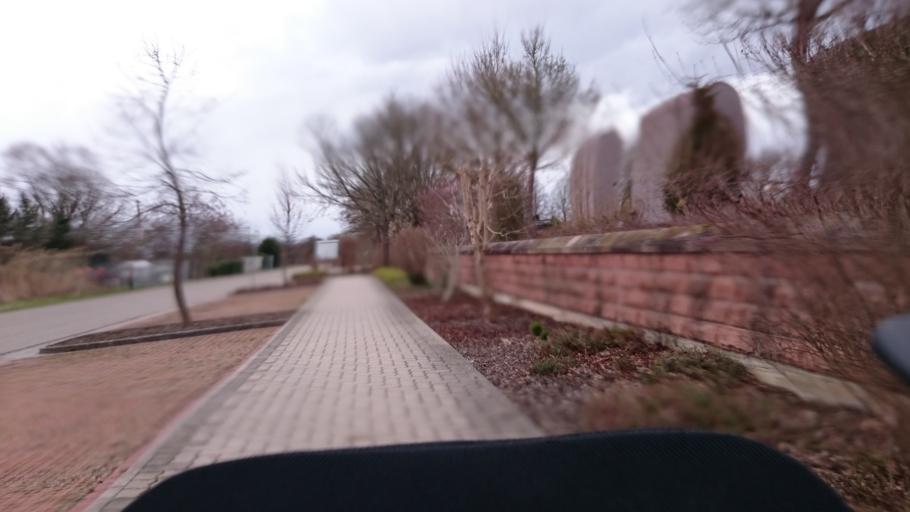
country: DE
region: Rheinland-Pfalz
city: Worth am Rhein
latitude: 49.0271
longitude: 8.2868
